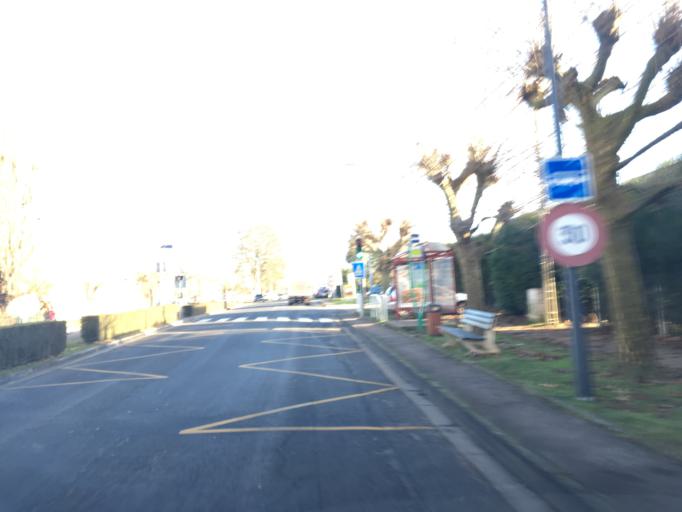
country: FR
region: Haute-Normandie
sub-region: Departement de l'Eure
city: Gaillon
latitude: 49.1585
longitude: 1.3437
